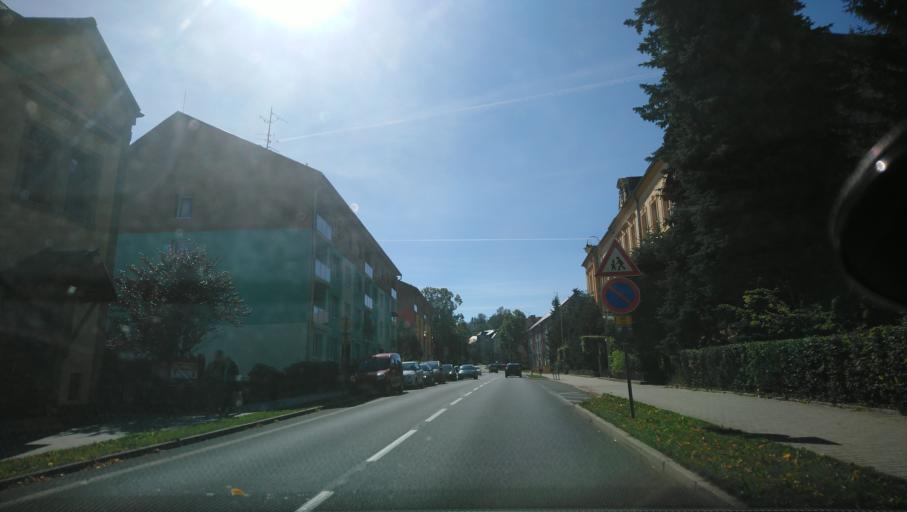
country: CZ
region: Ustecky
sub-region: Okres Chomutov
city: Vejprty
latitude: 50.4944
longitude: 13.0303
